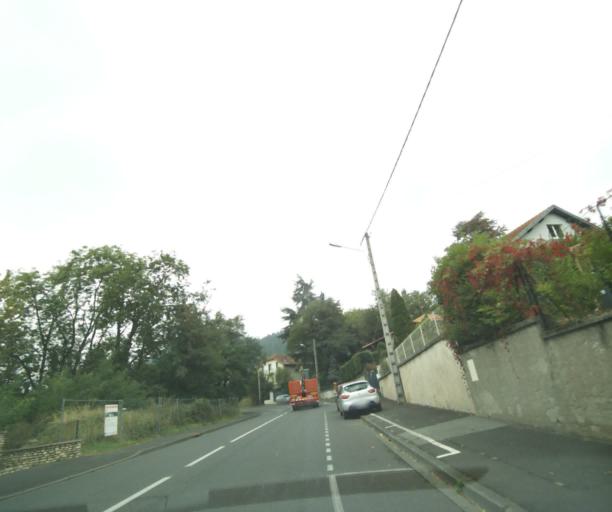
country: FR
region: Auvergne
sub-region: Departement du Puy-de-Dome
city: Ceyrat
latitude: 45.7429
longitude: 3.0593
